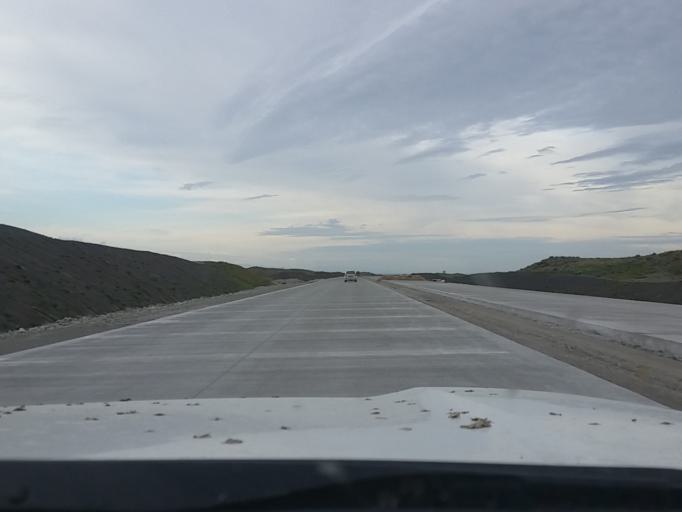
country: KZ
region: Almaty Oblysy
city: Zharkent
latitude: 44.1743
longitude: 80.3249
